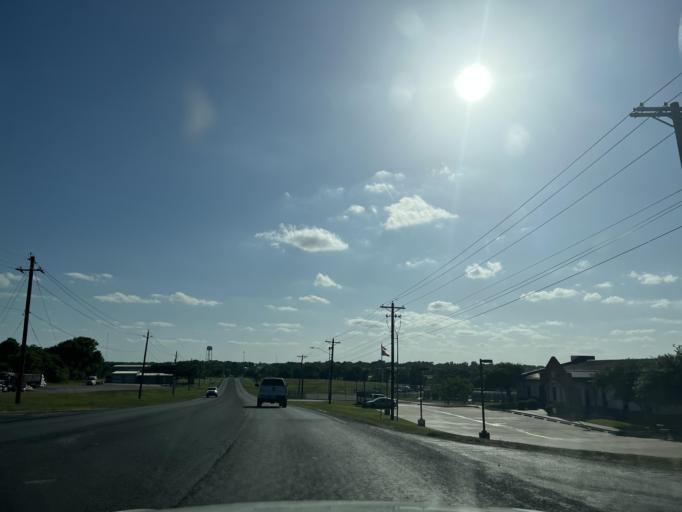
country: US
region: Texas
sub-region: Washington County
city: Brenham
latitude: 30.1791
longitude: -96.3881
